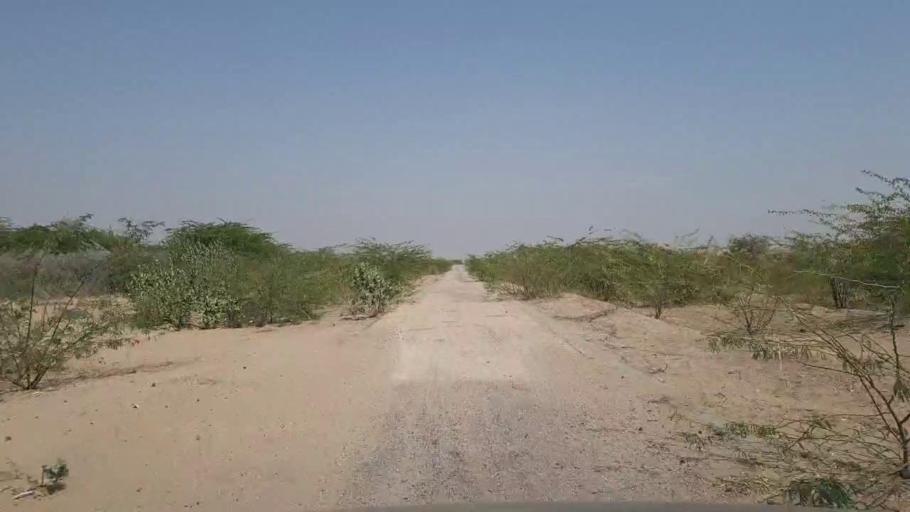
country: PK
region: Sindh
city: Chor
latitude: 25.5794
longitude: 70.1921
